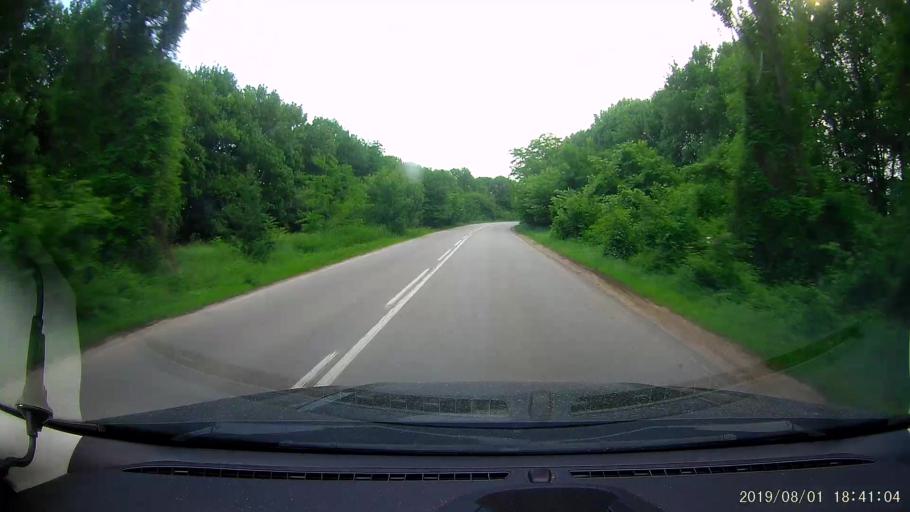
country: BG
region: Shumen
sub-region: Obshtina Khitrino
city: Gara Khitrino
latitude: 43.3525
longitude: 26.9234
